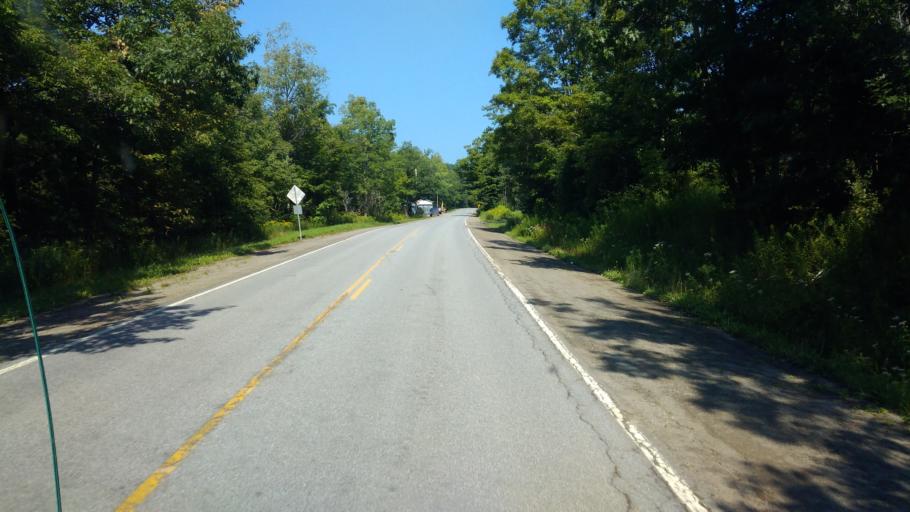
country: US
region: New York
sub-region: Allegany County
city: Bolivar
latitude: 42.0922
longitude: -78.1688
